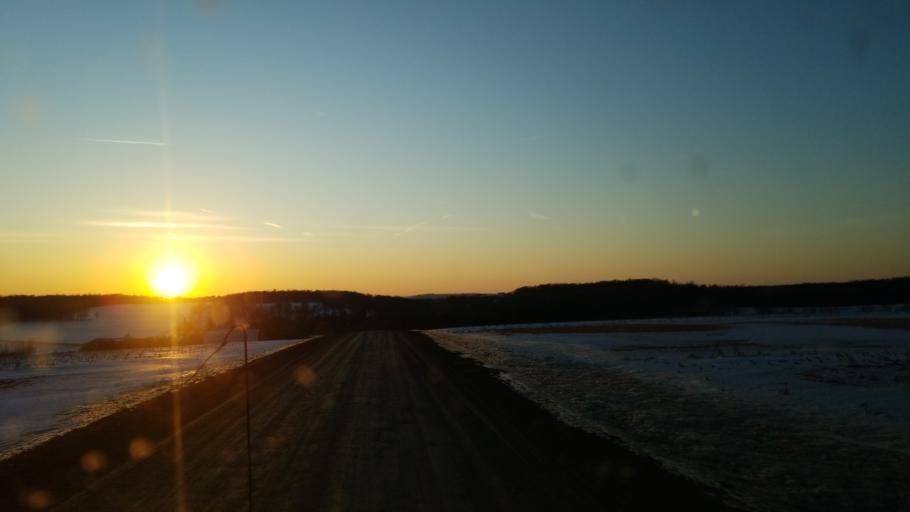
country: US
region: Pennsylvania
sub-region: Tioga County
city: Westfield
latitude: 42.0128
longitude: -77.6724
